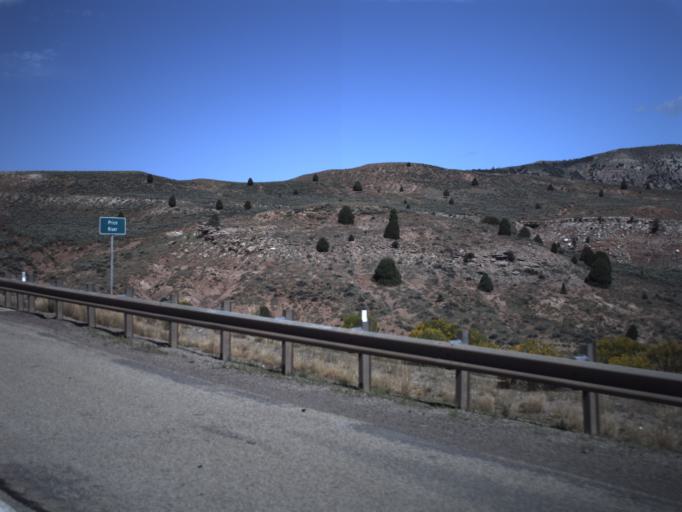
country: US
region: Utah
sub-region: Carbon County
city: Helper
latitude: 39.8437
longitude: -110.9957
